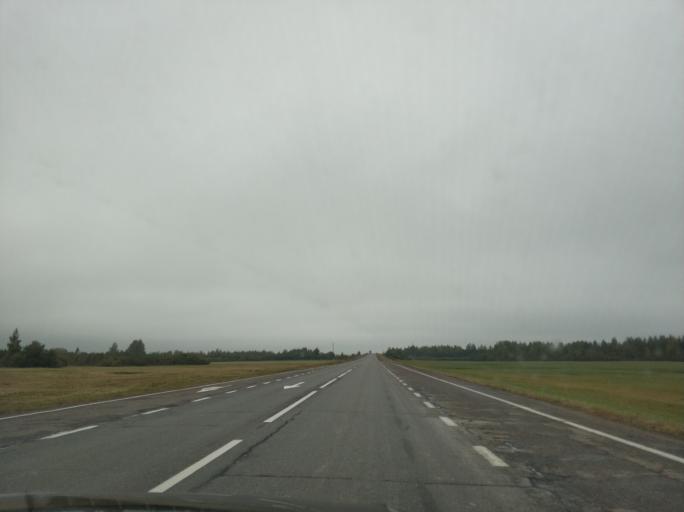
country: BY
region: Vitebsk
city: Chashniki
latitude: 55.3437
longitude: 29.3561
